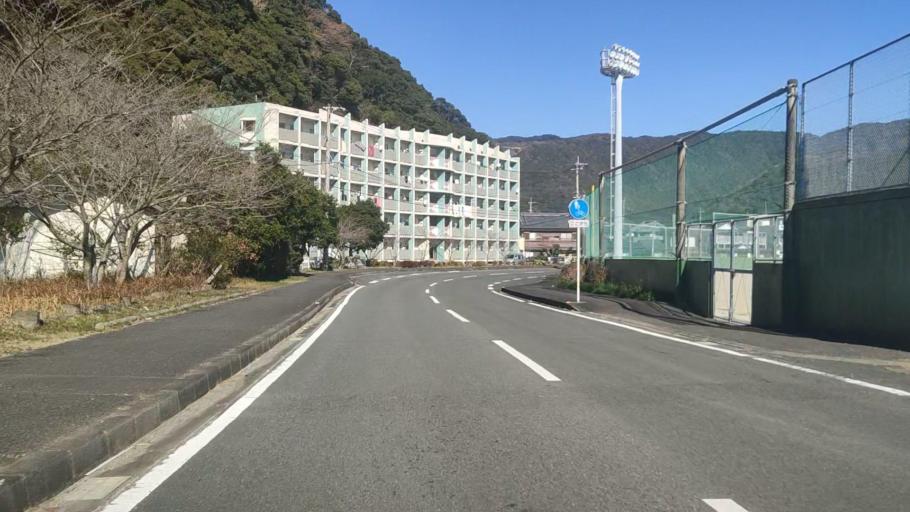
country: JP
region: Oita
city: Saiki
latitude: 32.8002
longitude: 131.9200
